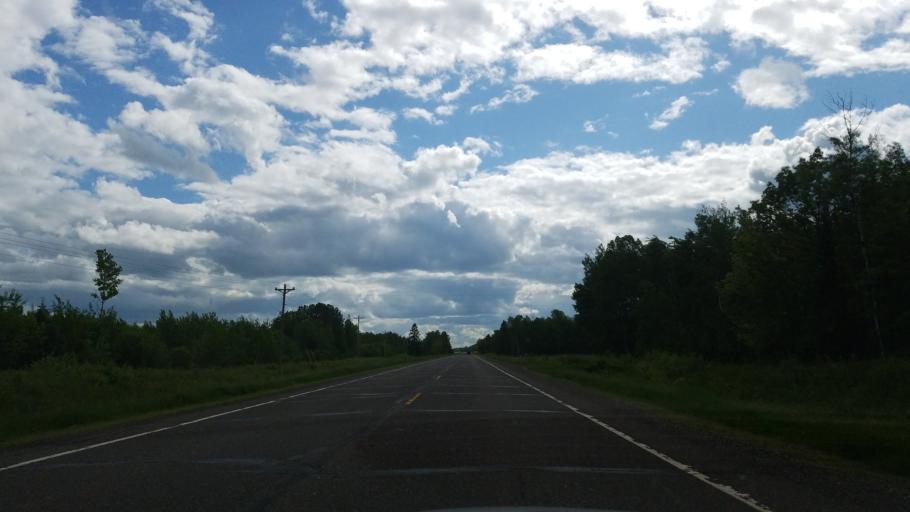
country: US
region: Wisconsin
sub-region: Washburn County
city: Spooner
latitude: 46.1975
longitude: -92.1637
